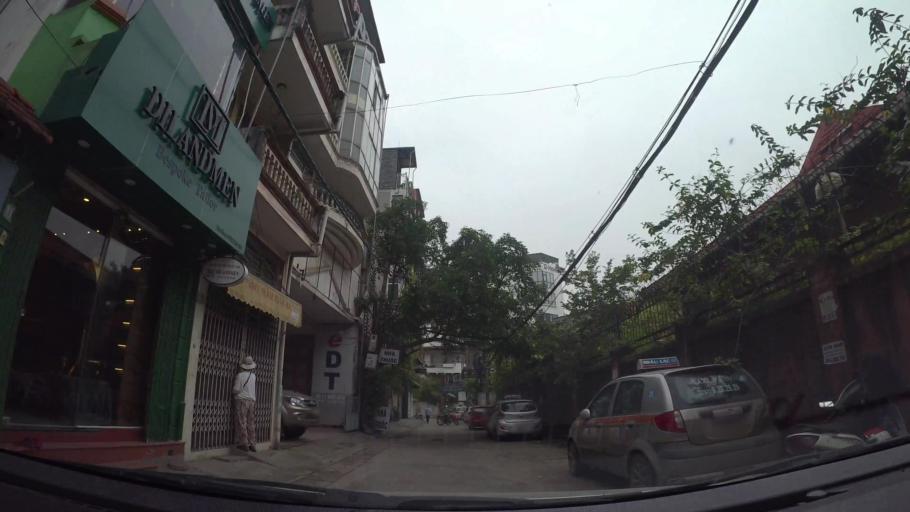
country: VN
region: Ha Noi
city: Dong Da
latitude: 21.0325
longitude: 105.8210
